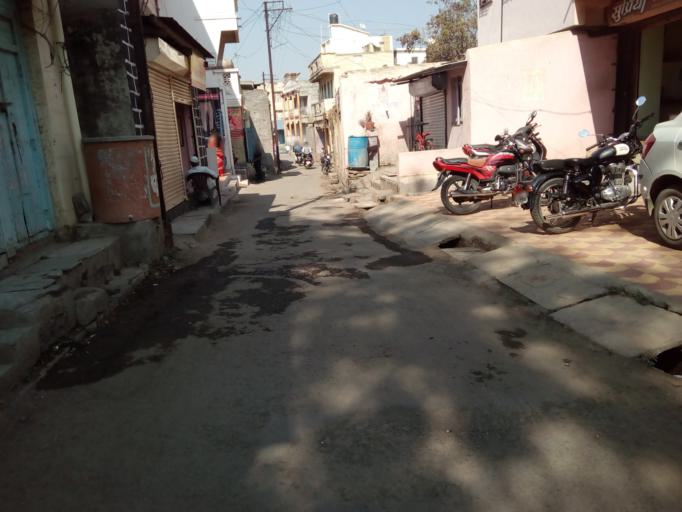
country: IN
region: Maharashtra
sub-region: Solapur
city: Sangola
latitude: 17.4370
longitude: 75.1932
